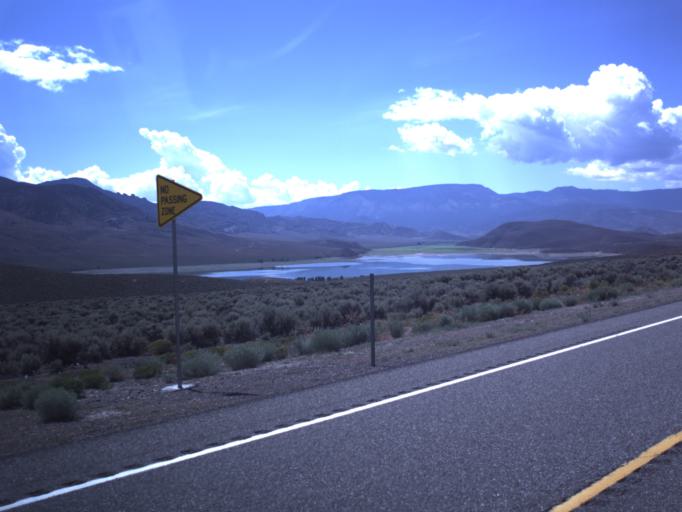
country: US
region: Utah
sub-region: Piute County
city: Junction
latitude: 38.3132
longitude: -112.2217
